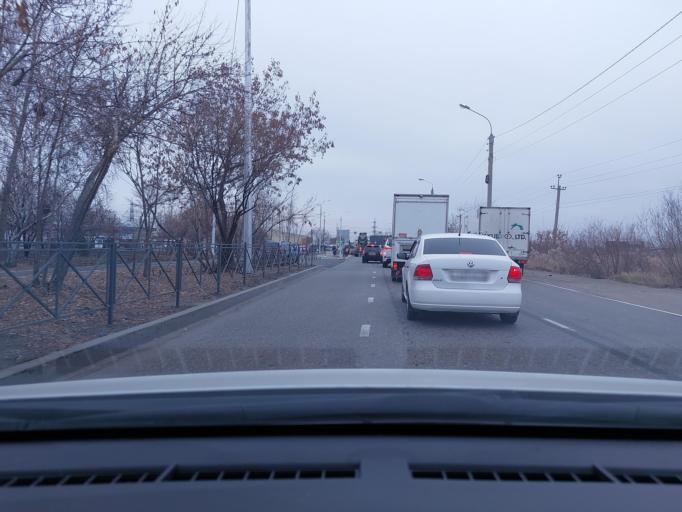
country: RU
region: Irkutsk
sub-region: Irkutskiy Rayon
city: Irkutsk
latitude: 52.3299
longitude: 104.2319
